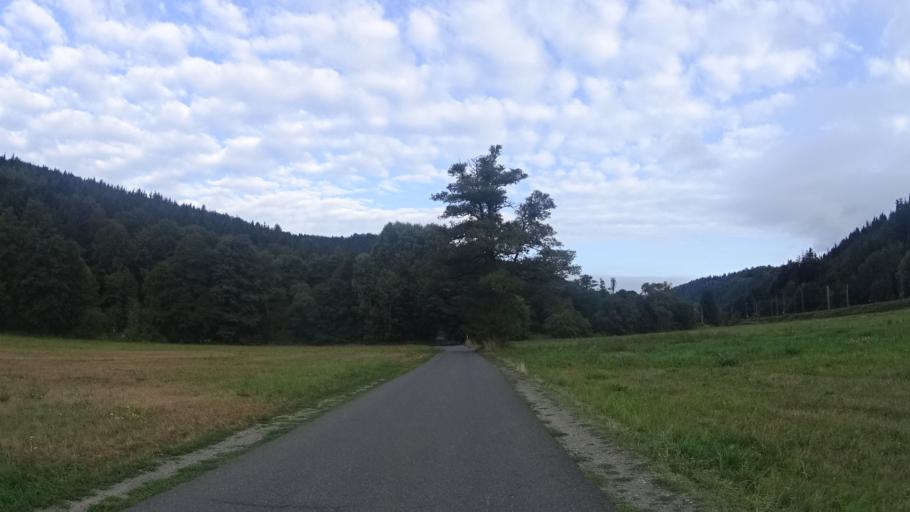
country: CZ
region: Olomoucky
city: Zabreh
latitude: 49.8663
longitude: 16.7938
